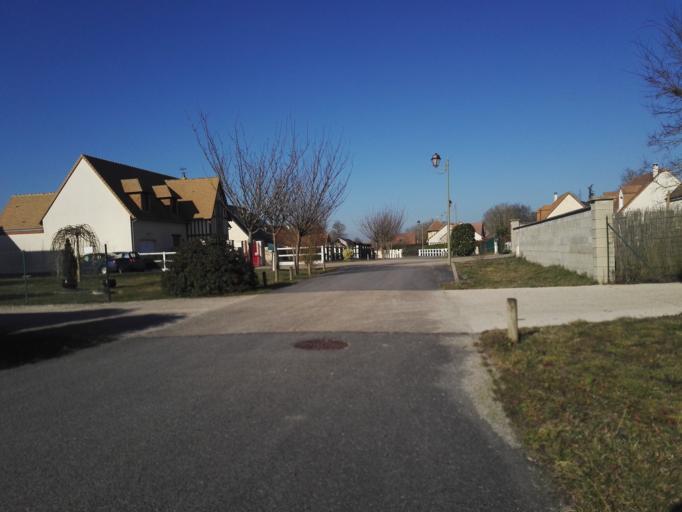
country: FR
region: Haute-Normandie
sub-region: Departement de l'Eure
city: Pacy-sur-Eure
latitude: 49.0062
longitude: 1.4226
